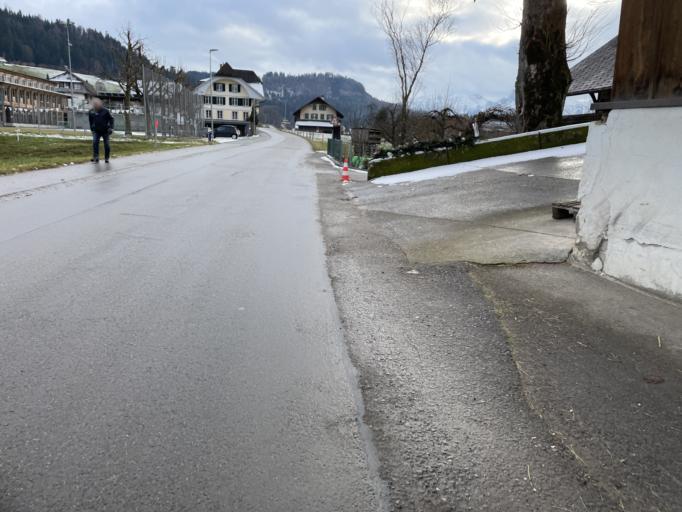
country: CH
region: Lucerne
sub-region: Entlebuch District
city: Oberdiessbach
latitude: 46.8187
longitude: 7.6138
